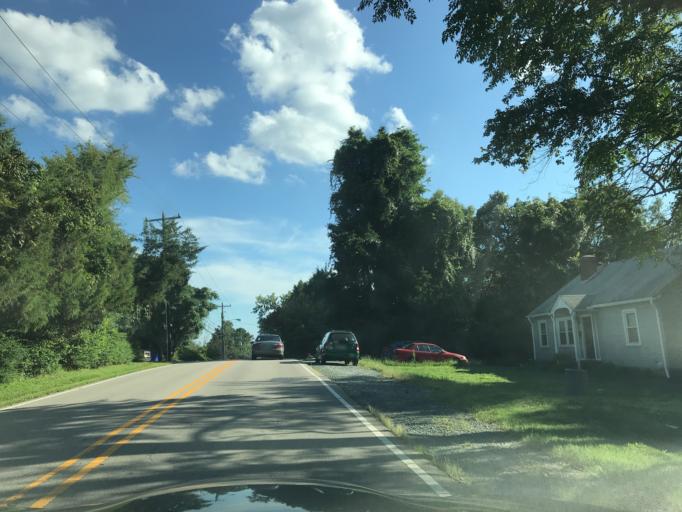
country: US
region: North Carolina
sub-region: Orange County
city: Carrboro
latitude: 35.9082
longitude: -79.0724
